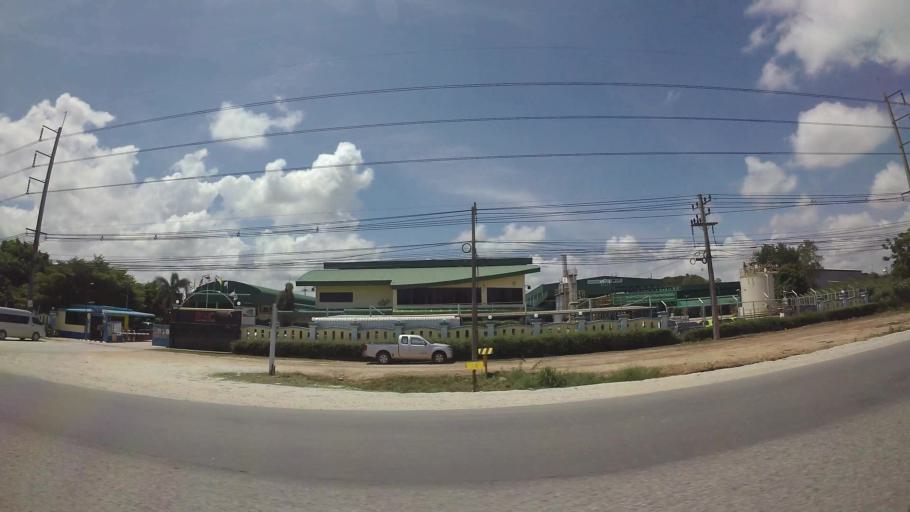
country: TH
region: Rayong
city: Rayong
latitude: 12.7214
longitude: 101.2217
